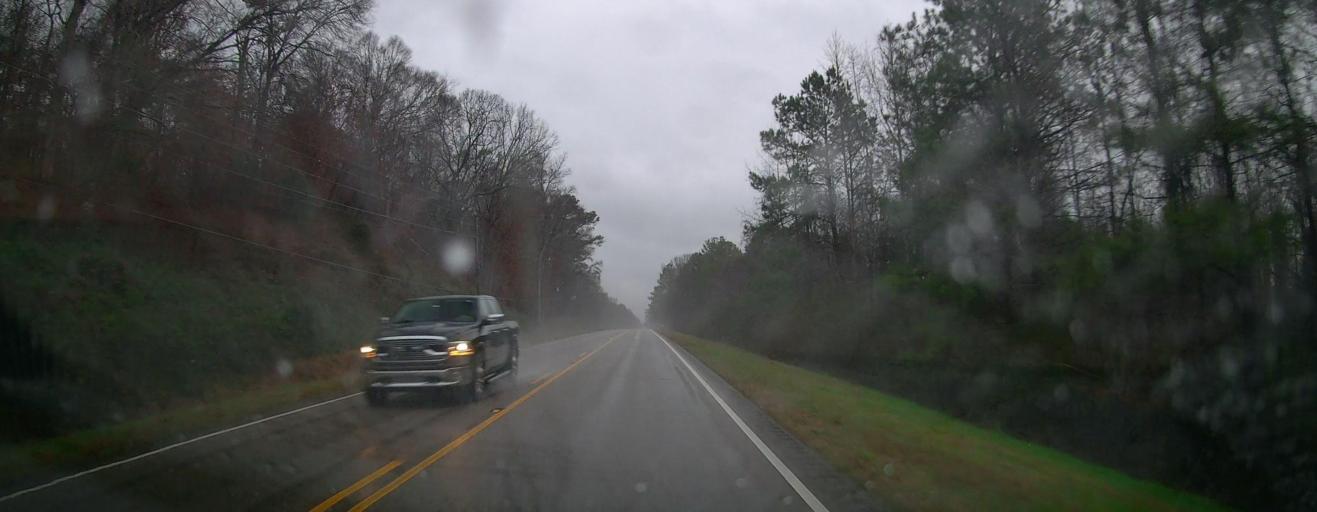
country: US
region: Alabama
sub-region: Autauga County
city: Prattville
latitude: 32.4771
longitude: -86.5256
